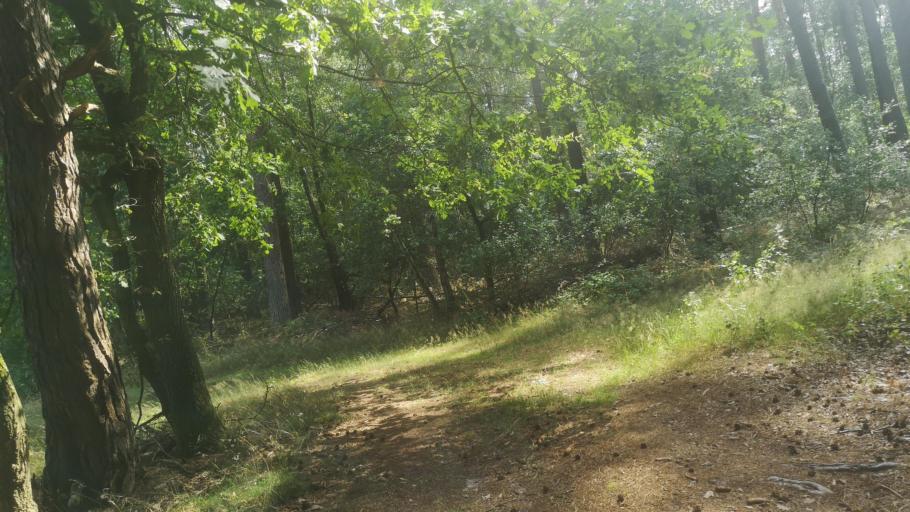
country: DE
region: Lower Saxony
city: Dahlem
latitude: 53.2209
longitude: 10.7443
